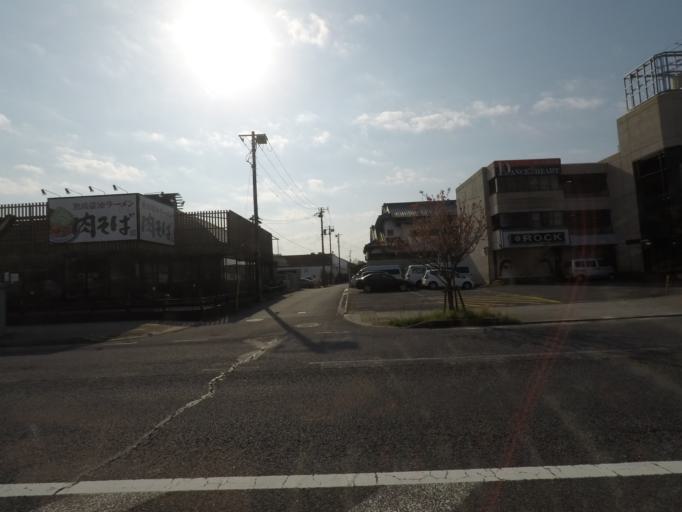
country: JP
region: Chiba
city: Narita
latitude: 35.7831
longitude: 140.3268
